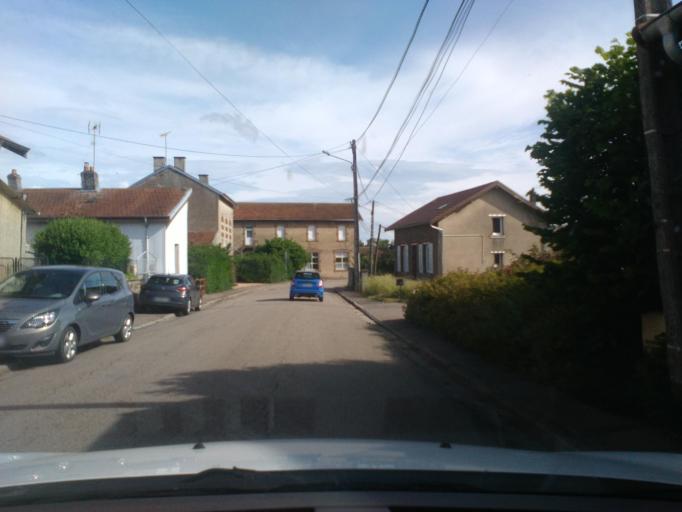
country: FR
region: Lorraine
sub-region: Departement de Meurthe-et-Moselle
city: Baccarat
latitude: 48.4908
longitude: 6.6957
